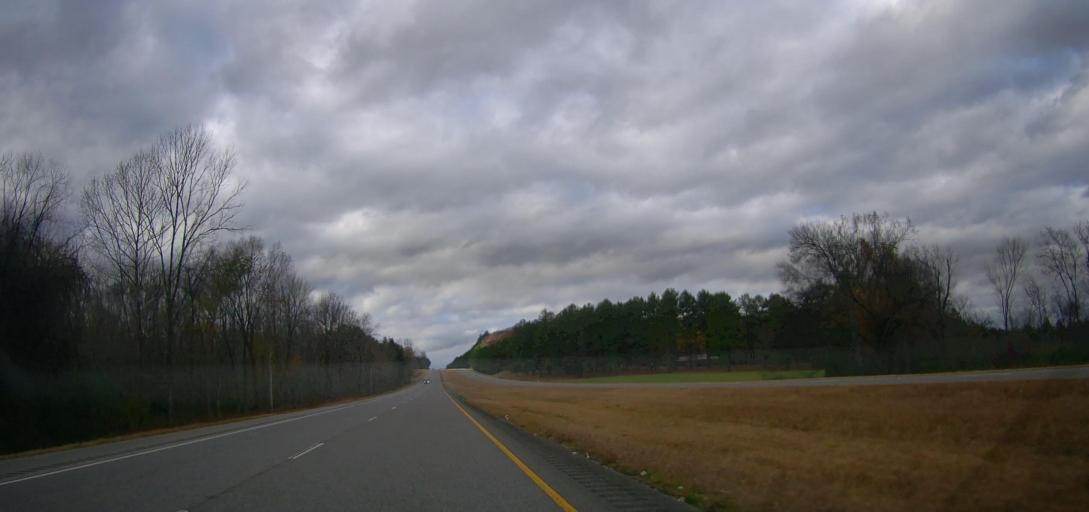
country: US
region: Alabama
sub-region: Lawrence County
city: Town Creek
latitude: 34.6121
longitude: -87.4584
